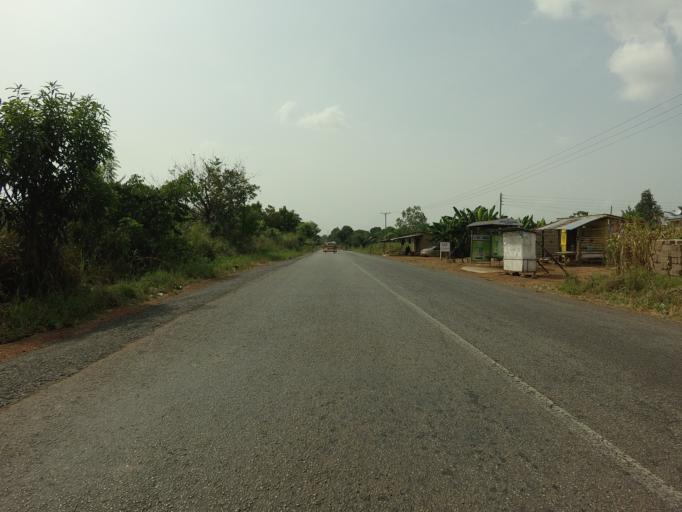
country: GH
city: Akropong
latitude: 6.2642
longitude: 0.1360
